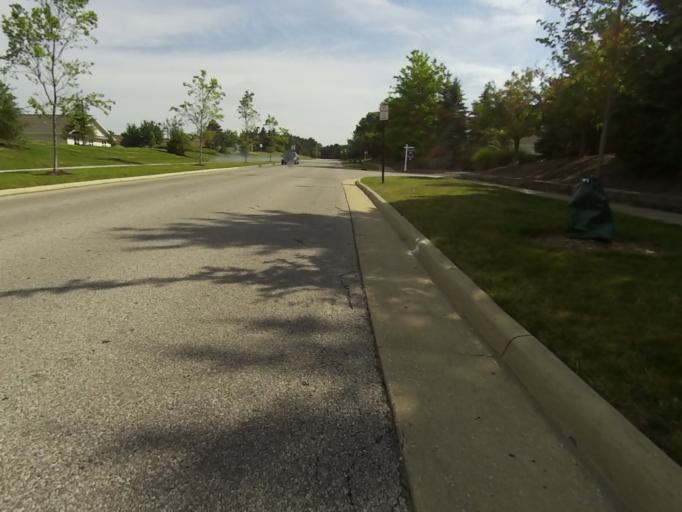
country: US
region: Ohio
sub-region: Summit County
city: Hudson
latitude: 41.1998
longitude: -81.4342
